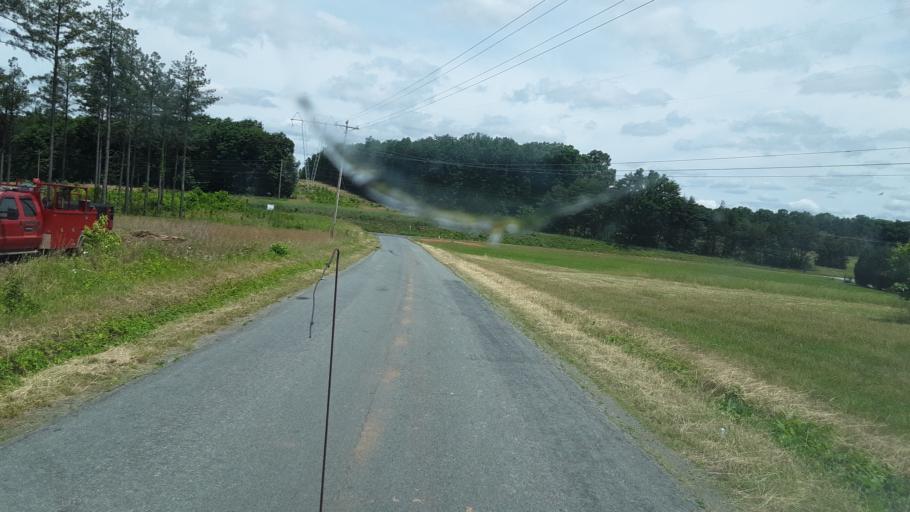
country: US
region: Virginia
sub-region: Pittsylvania County
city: Chatham
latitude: 36.8351
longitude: -79.4587
